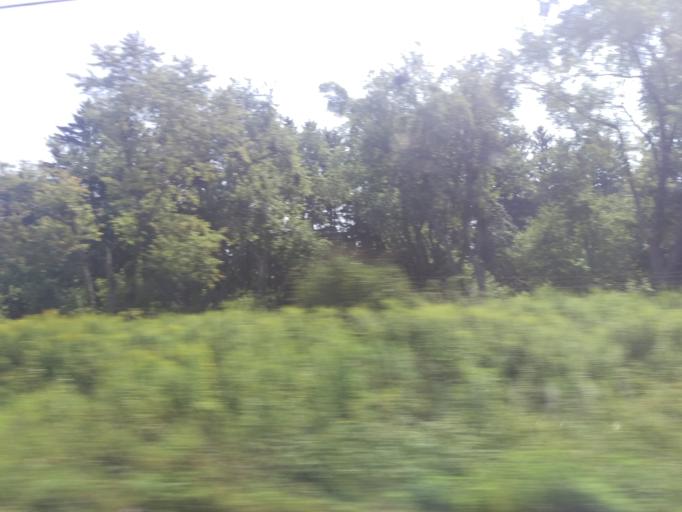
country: CA
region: Ontario
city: Ajax
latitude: 43.7966
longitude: -79.1168
